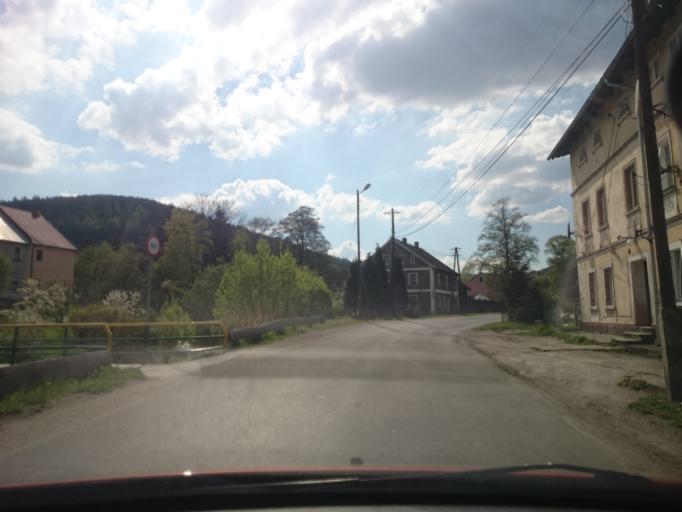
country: PL
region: Lower Silesian Voivodeship
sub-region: Powiat klodzki
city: Bystrzyca Klodzka
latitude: 50.3050
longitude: 16.6113
